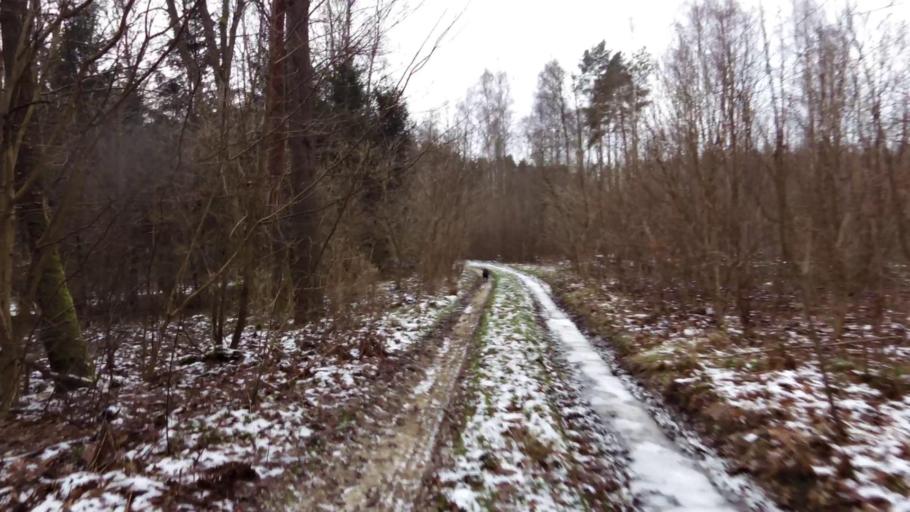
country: PL
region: West Pomeranian Voivodeship
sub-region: Powiat drawski
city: Drawsko Pomorskie
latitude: 53.5415
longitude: 15.7023
